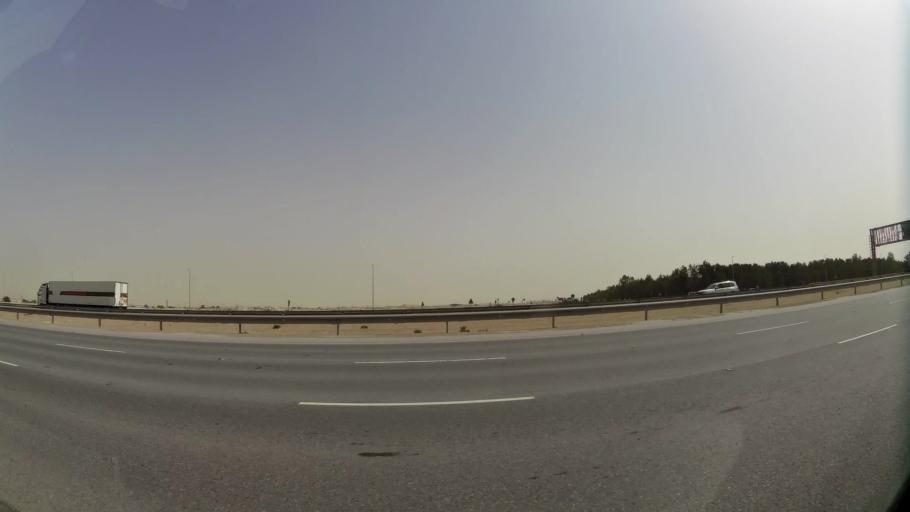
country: QA
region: Baladiyat ar Rayyan
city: Ar Rayyan
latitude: 25.1655
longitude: 51.3069
